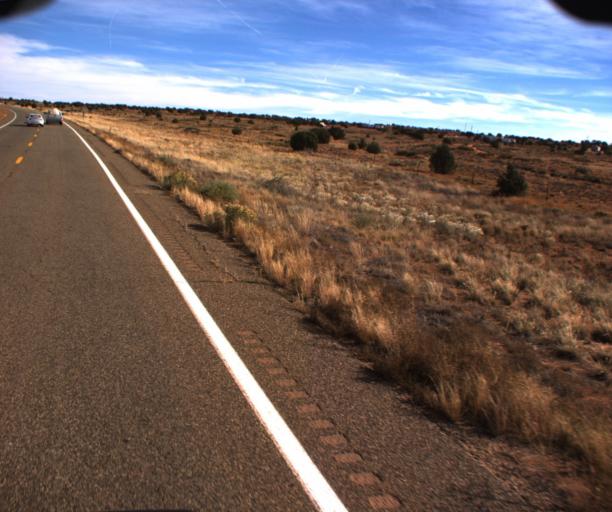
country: US
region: Arizona
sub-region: Coconino County
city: Kaibito
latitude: 36.5827
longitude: -111.1076
